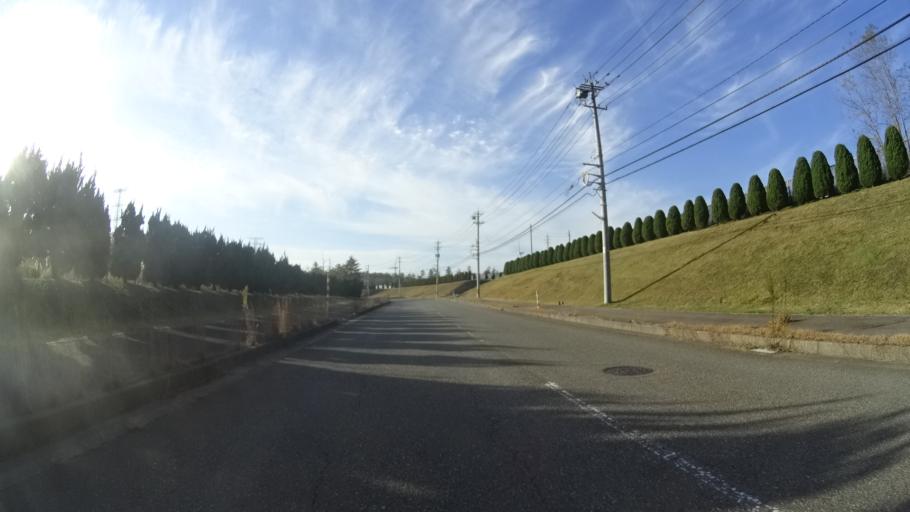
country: JP
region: Ishikawa
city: Hakui
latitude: 37.0684
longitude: 136.7570
